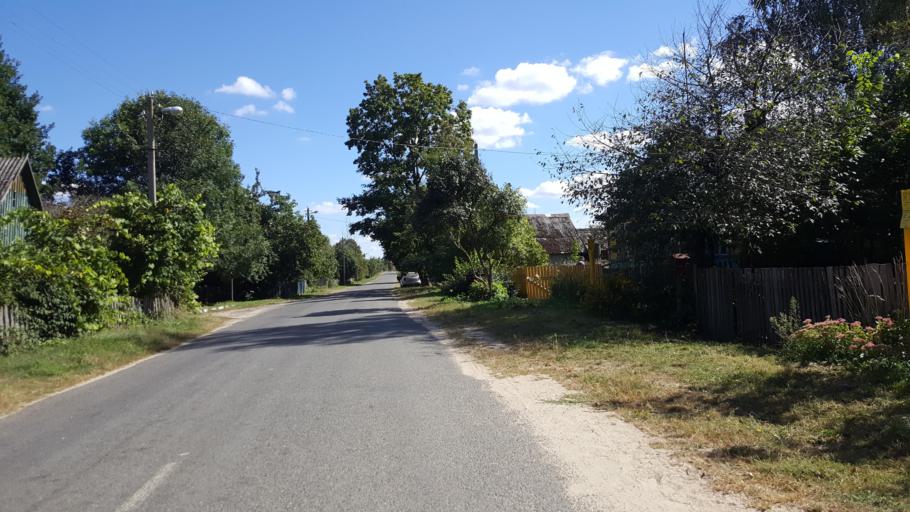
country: BY
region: Brest
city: Vysokaye
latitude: 52.2624
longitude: 23.4092
